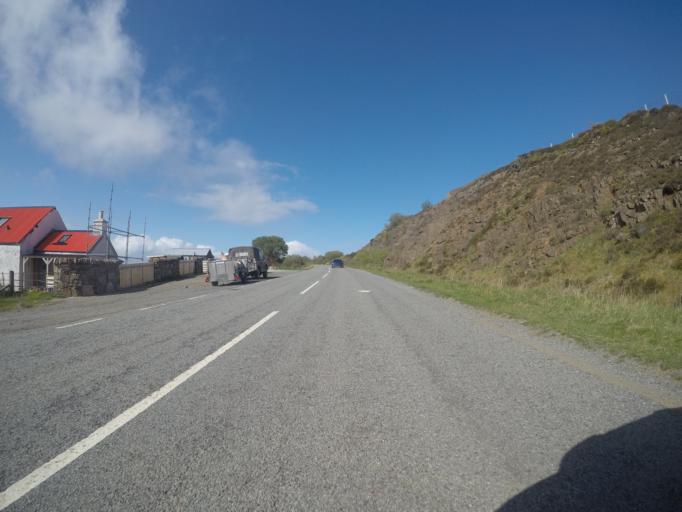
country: GB
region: Scotland
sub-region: Highland
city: Portree
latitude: 57.5855
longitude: -6.1573
